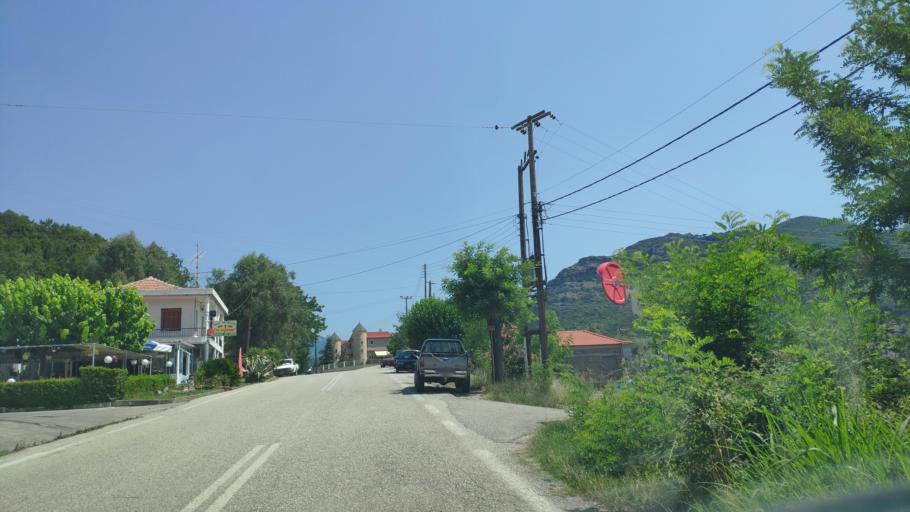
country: GR
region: West Greece
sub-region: Nomos Aitolias kai Akarnanias
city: Sardinia
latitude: 38.8962
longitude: 21.3484
